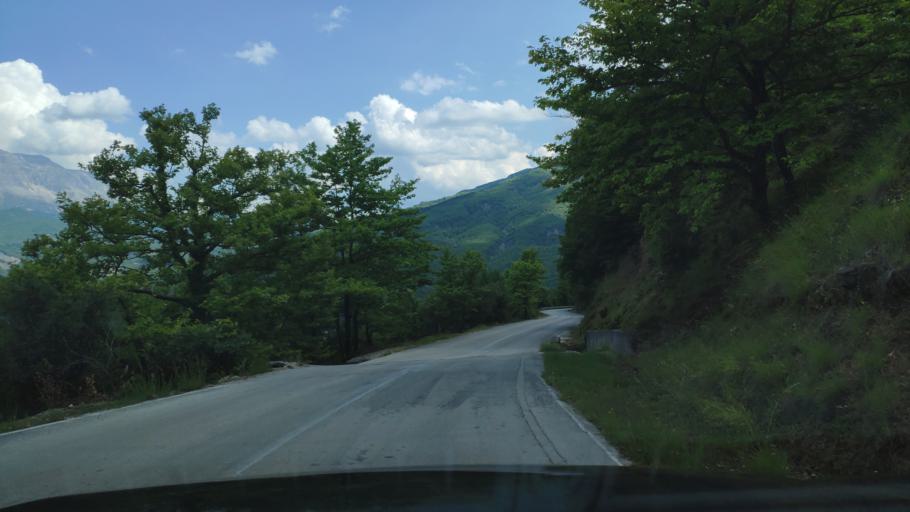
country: GR
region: Epirus
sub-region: Nomos Artas
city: Agios Dimitrios
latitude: 39.4600
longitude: 21.0278
